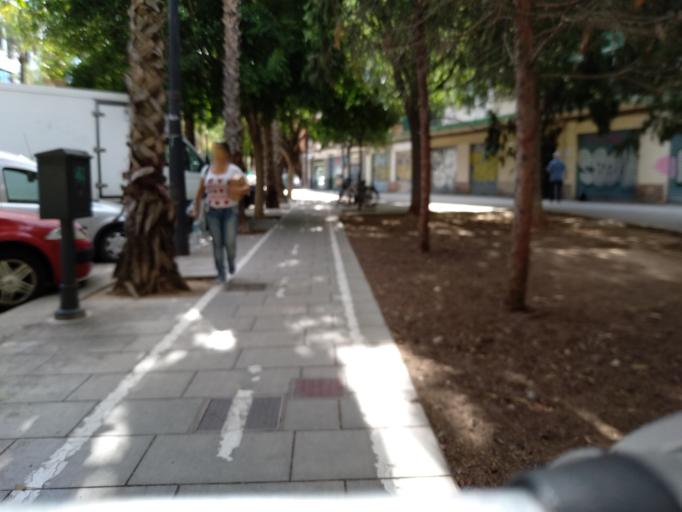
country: ES
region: Valencia
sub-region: Provincia de Valencia
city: Valencia
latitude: 39.4858
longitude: -0.3800
